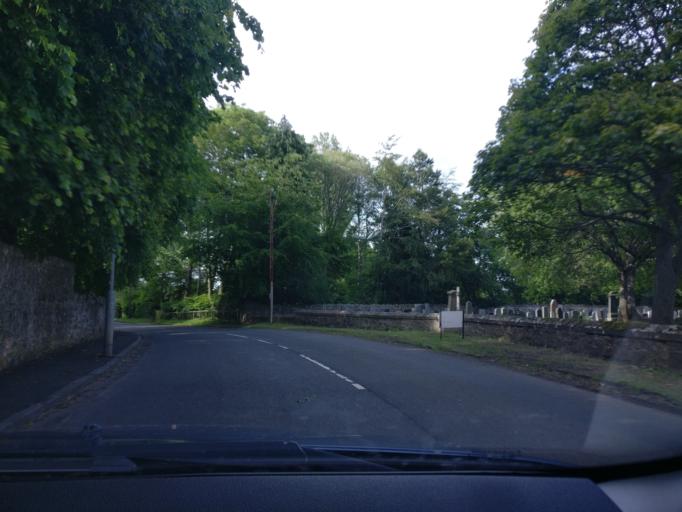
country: GB
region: Scotland
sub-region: East Lothian
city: Haddington
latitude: 55.9040
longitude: -2.7460
